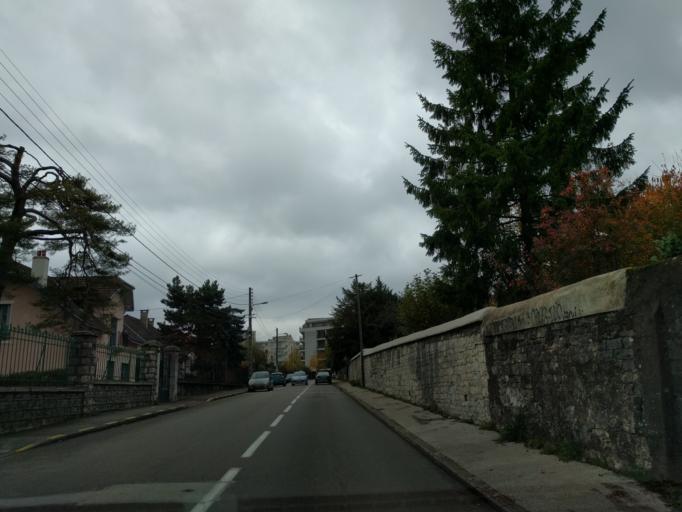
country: FR
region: Franche-Comte
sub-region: Departement du Doubs
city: Besancon
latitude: 47.2524
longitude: 6.0262
